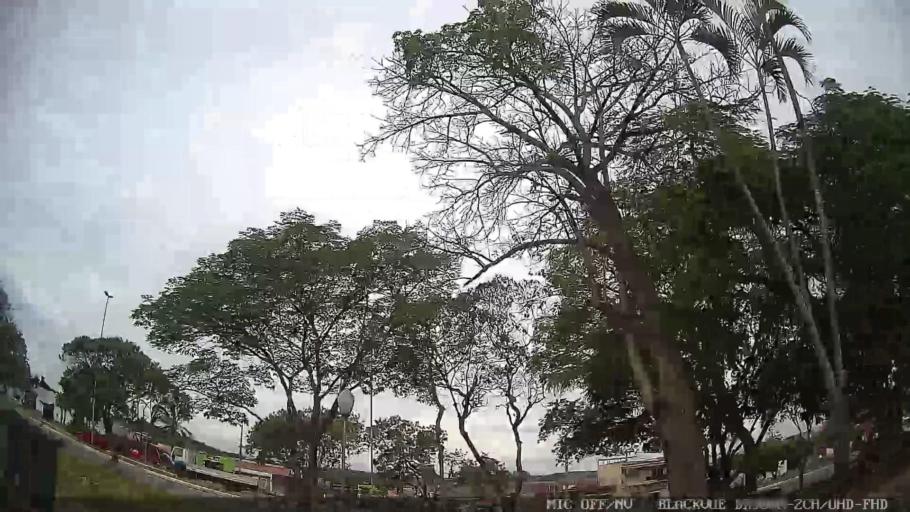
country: BR
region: Sao Paulo
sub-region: Salto
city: Salto
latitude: -23.2143
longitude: -47.2811
